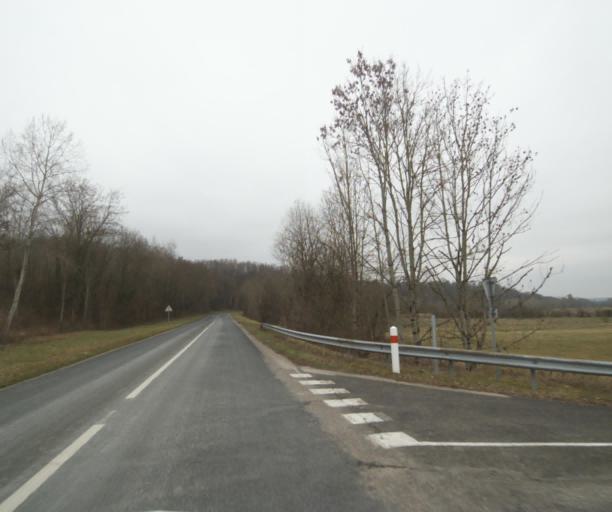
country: FR
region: Champagne-Ardenne
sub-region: Departement de la Haute-Marne
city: Bienville
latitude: 48.5684
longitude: 5.0403
